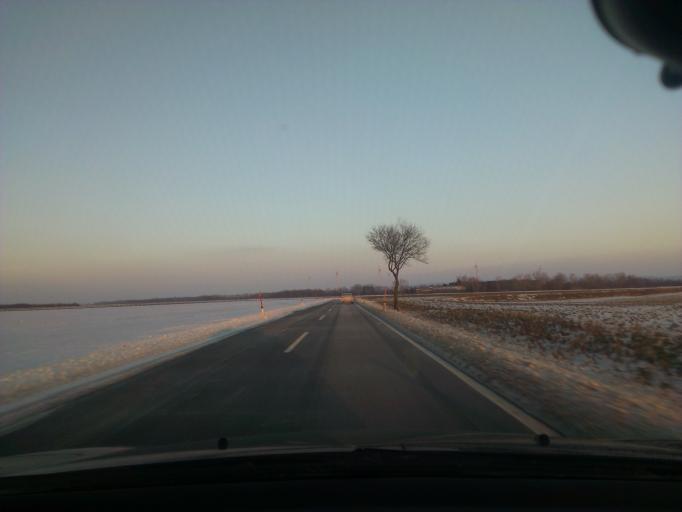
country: AT
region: Lower Austria
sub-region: Politischer Bezirk Baden
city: Mitterndorf an der Fischa
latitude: 47.9614
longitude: 16.4466
